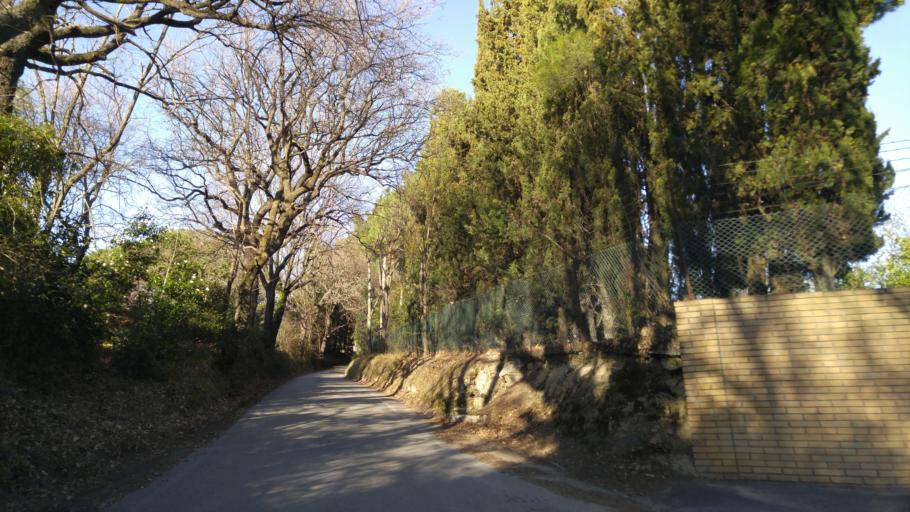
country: IT
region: The Marches
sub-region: Provincia di Pesaro e Urbino
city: Fenile
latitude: 43.8502
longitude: 12.9243
